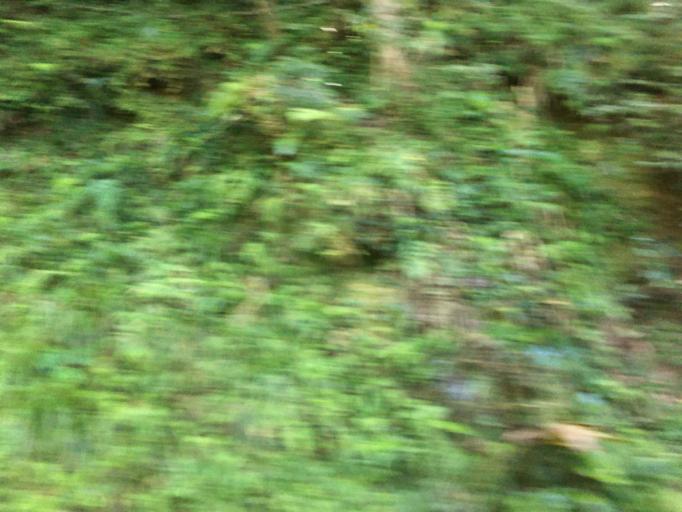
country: TW
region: Taiwan
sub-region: Yilan
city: Yilan
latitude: 24.6200
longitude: 121.4809
